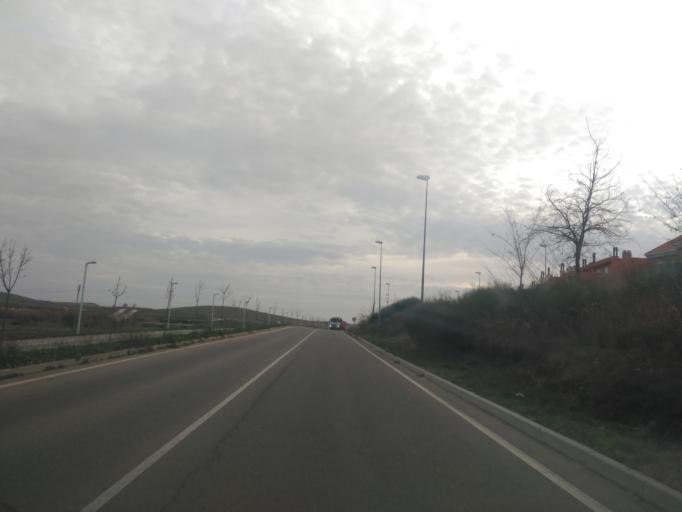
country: ES
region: Castille and Leon
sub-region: Provincia de Salamanca
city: Salamanca
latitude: 40.9474
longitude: -5.6783
